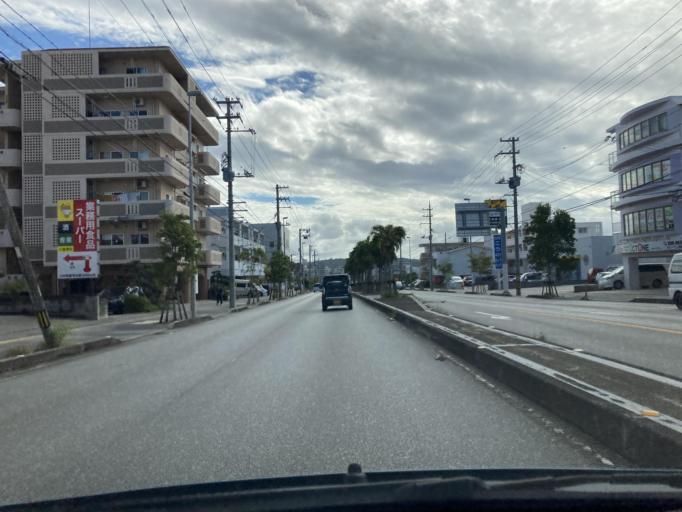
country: JP
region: Okinawa
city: Tomigusuku
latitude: 26.1623
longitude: 127.7234
